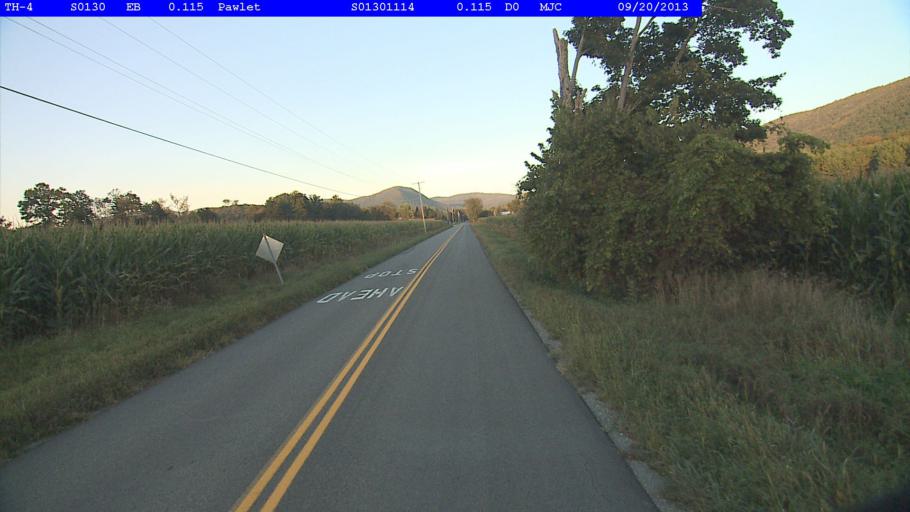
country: US
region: New York
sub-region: Washington County
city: Granville
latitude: 43.3523
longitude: -73.1509
